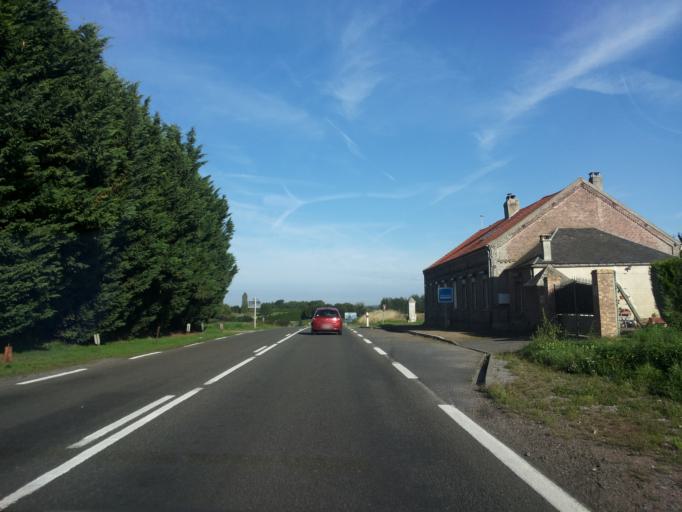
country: FR
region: Picardie
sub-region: Departement de l'Aisne
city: Charmes
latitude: 49.6415
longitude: 3.3988
